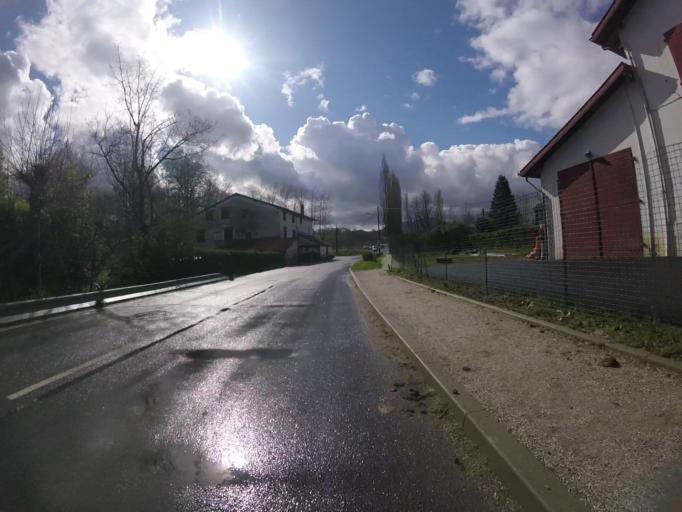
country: FR
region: Aquitaine
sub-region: Departement des Pyrenees-Atlantiques
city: Sare
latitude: 43.3107
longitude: -1.5726
